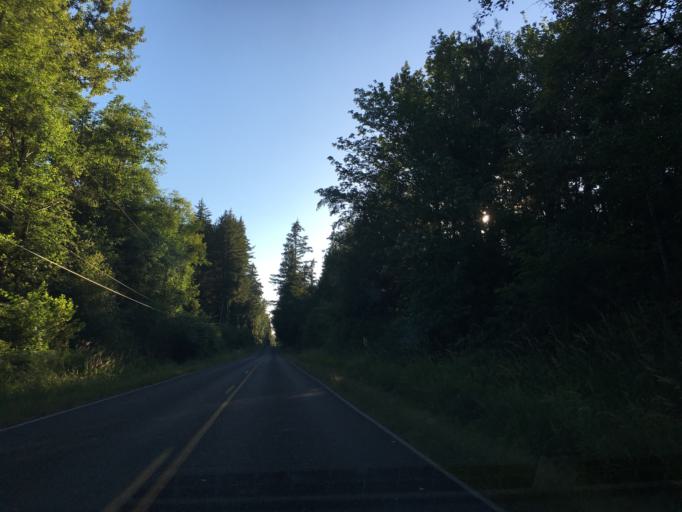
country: US
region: Washington
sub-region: Whatcom County
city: Geneva
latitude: 48.8183
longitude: -122.3601
